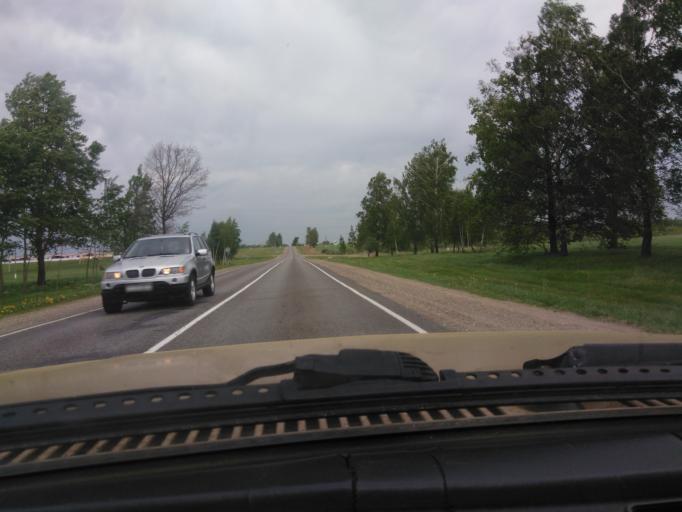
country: BY
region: Mogilev
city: Palykavichy Pyershyya
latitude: 54.0160
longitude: 30.3216
